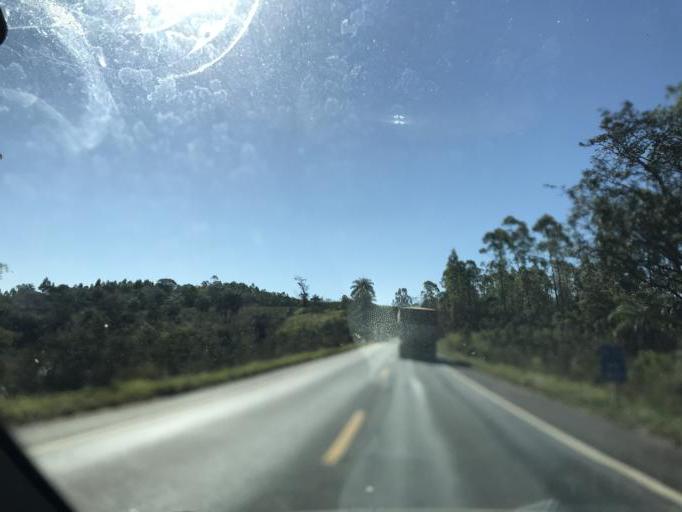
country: BR
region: Minas Gerais
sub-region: Bambui
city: Bambui
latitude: -19.8739
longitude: -45.9853
